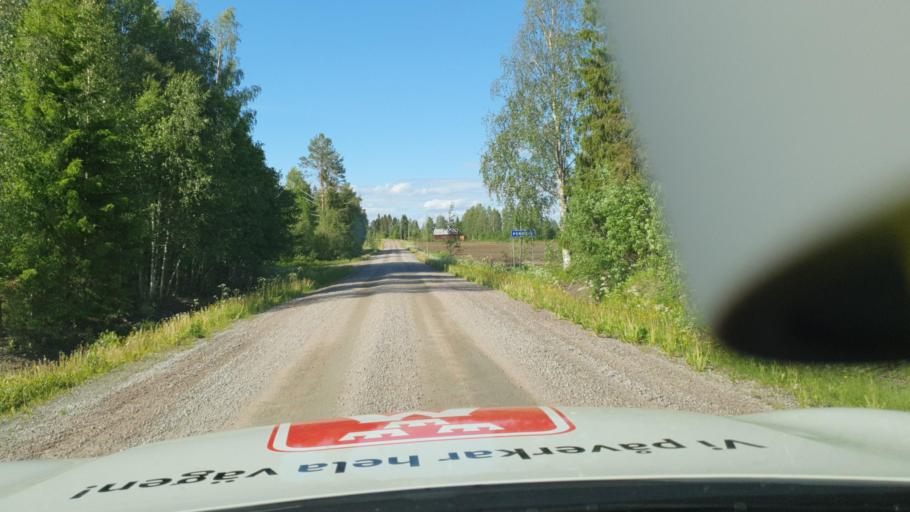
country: SE
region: Vaesterbotten
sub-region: Vannas Kommun
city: Vaennaes
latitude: 63.8243
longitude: 19.6278
